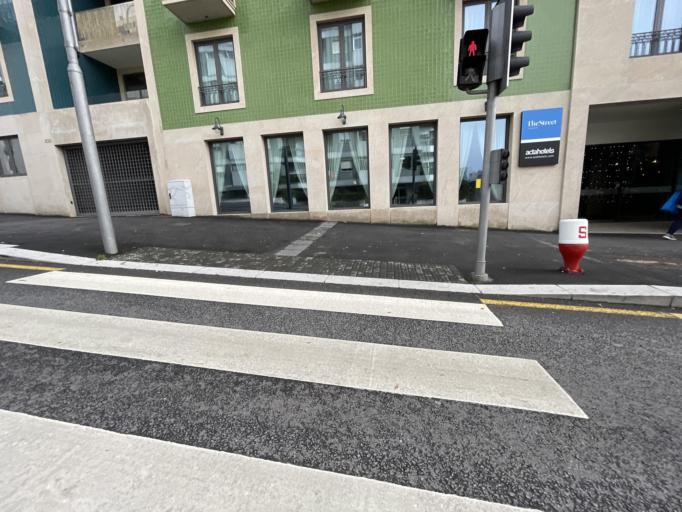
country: PT
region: Porto
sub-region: Porto
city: Porto
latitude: 41.1517
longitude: -8.5971
